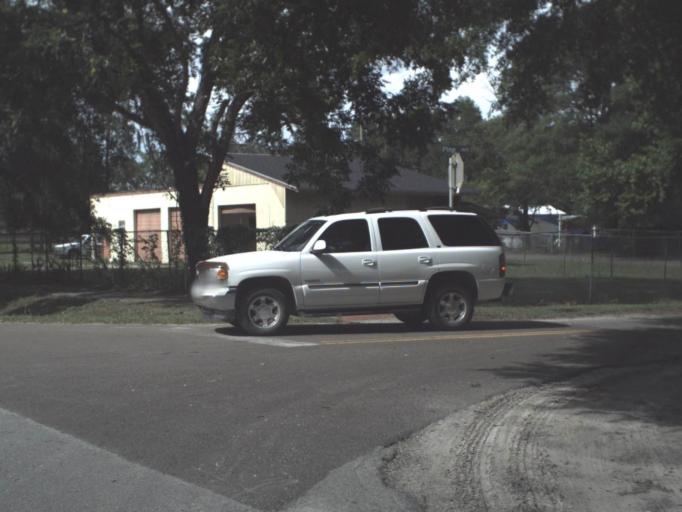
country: US
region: Florida
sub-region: Gilchrist County
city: Trenton
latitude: 29.7487
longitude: -82.8598
